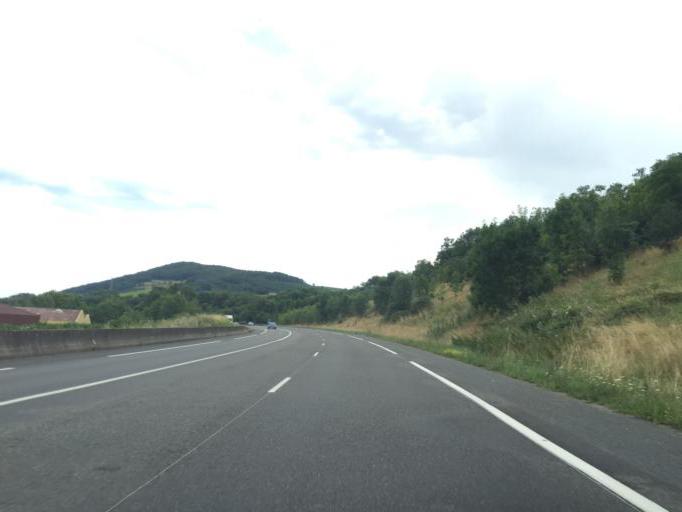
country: FR
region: Rhone-Alpes
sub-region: Departement du Rhone
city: Pontcharra-sur-Turdine
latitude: 45.8760
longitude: 4.4768
